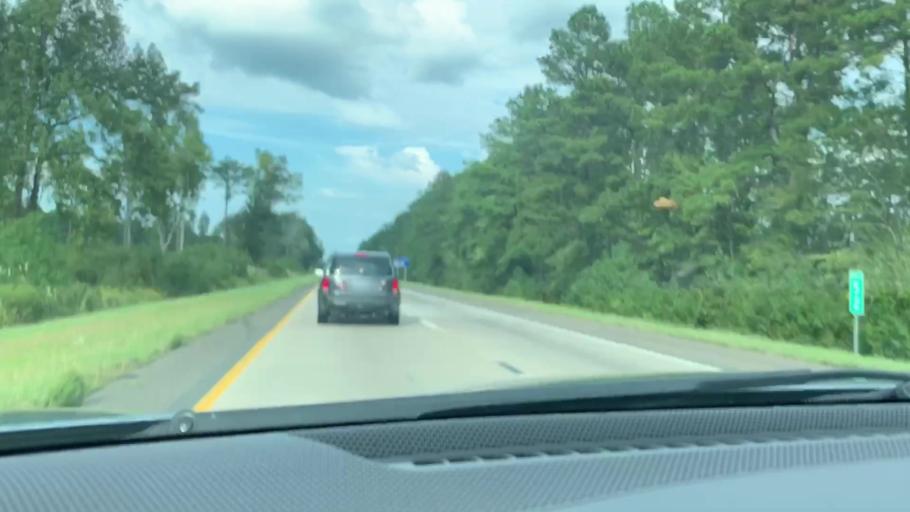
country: US
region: South Carolina
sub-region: Colleton County
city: Walterboro
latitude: 32.8600
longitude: -80.7276
